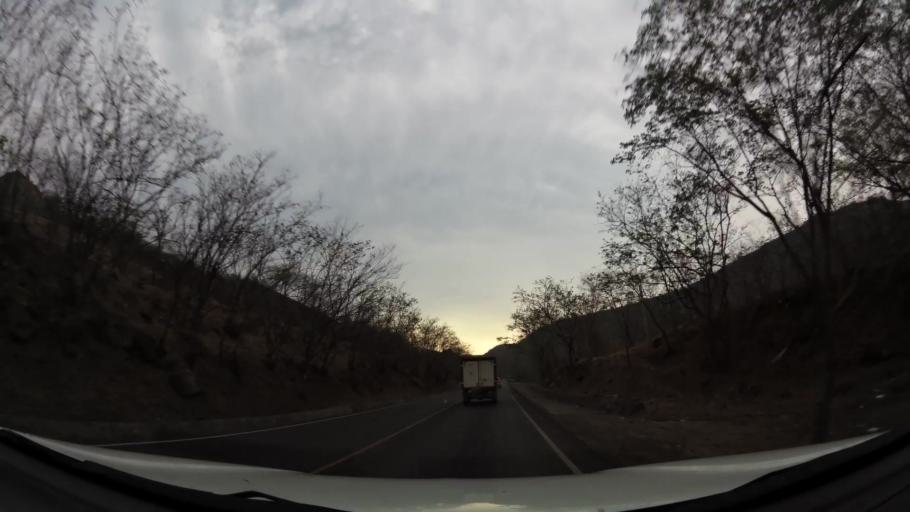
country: NI
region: Esteli
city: Esteli
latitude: 12.9387
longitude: -86.2176
